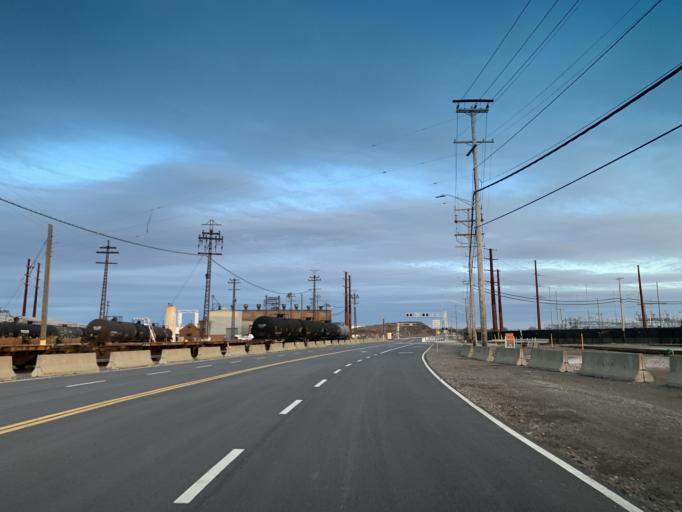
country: US
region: Maryland
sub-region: Baltimore County
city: Edgemere
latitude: 39.2267
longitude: -76.4826
